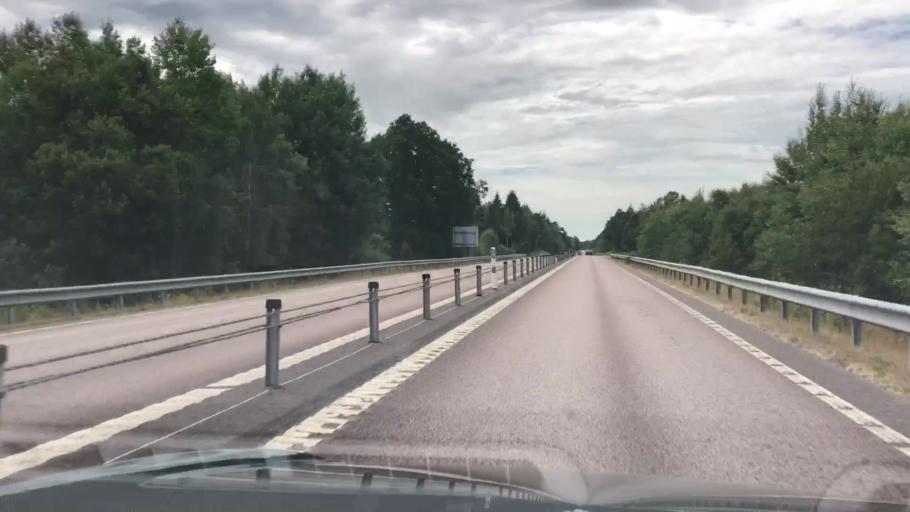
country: SE
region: Kalmar
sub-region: Torsas Kommun
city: Torsas
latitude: 56.2739
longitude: 15.9668
